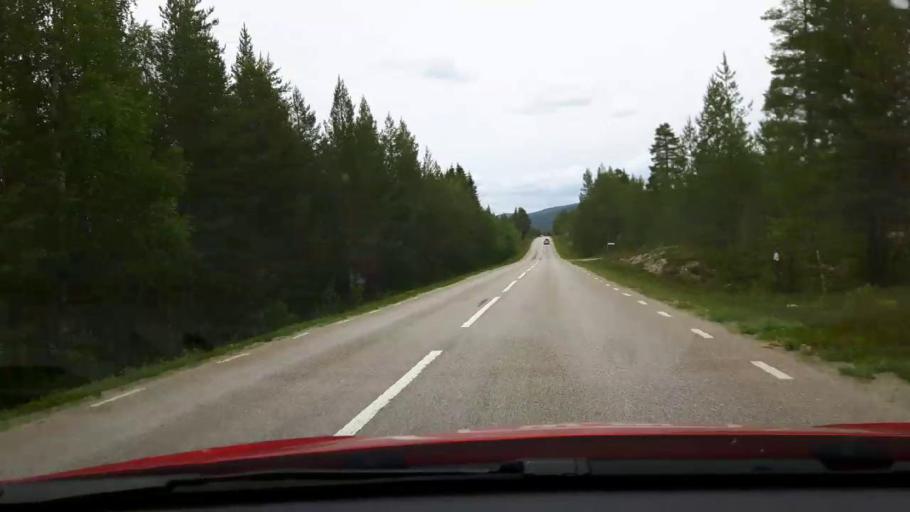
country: SE
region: Jaemtland
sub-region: Harjedalens Kommun
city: Sveg
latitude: 62.2482
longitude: 13.8428
